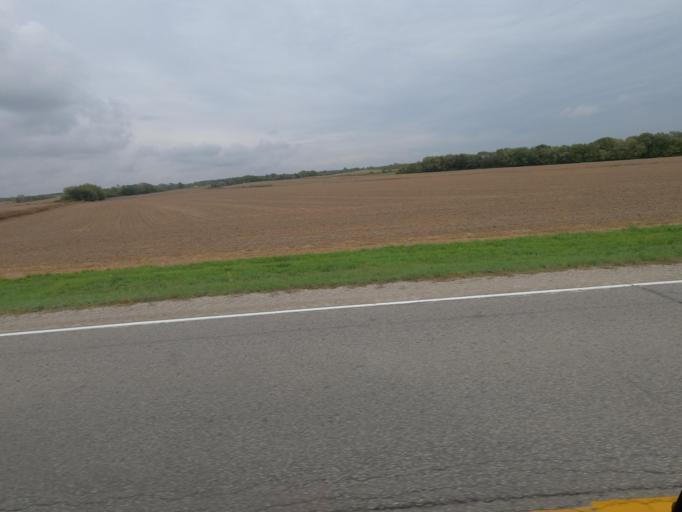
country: US
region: Iowa
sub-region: Jefferson County
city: Fairfield
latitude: 40.8953
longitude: -92.1836
